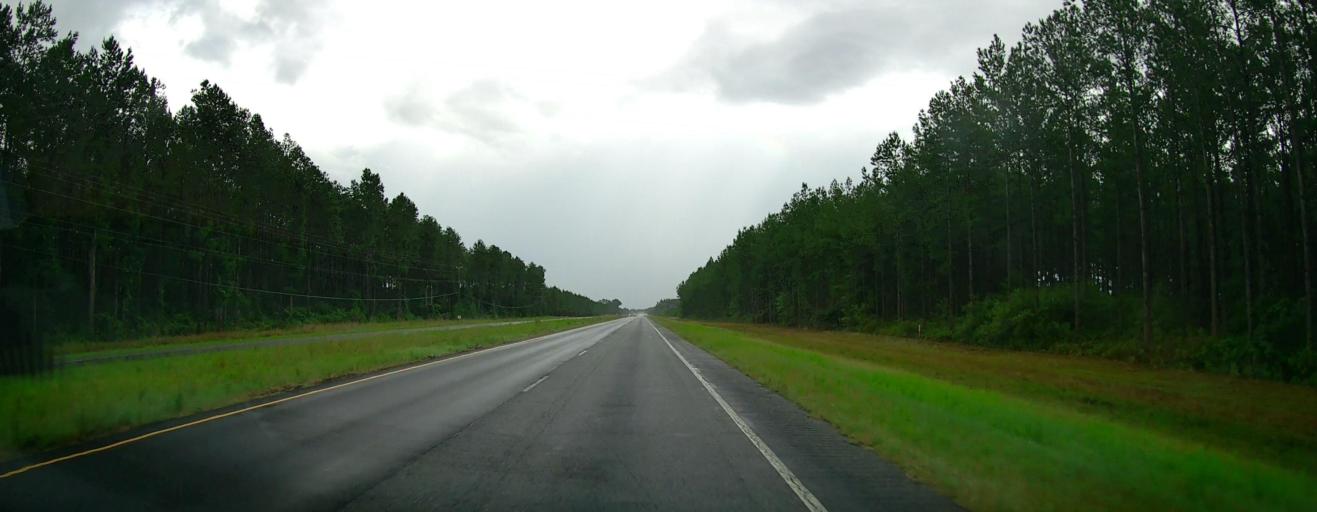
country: US
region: Georgia
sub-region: Ware County
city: Deenwood
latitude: 31.2600
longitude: -82.5087
